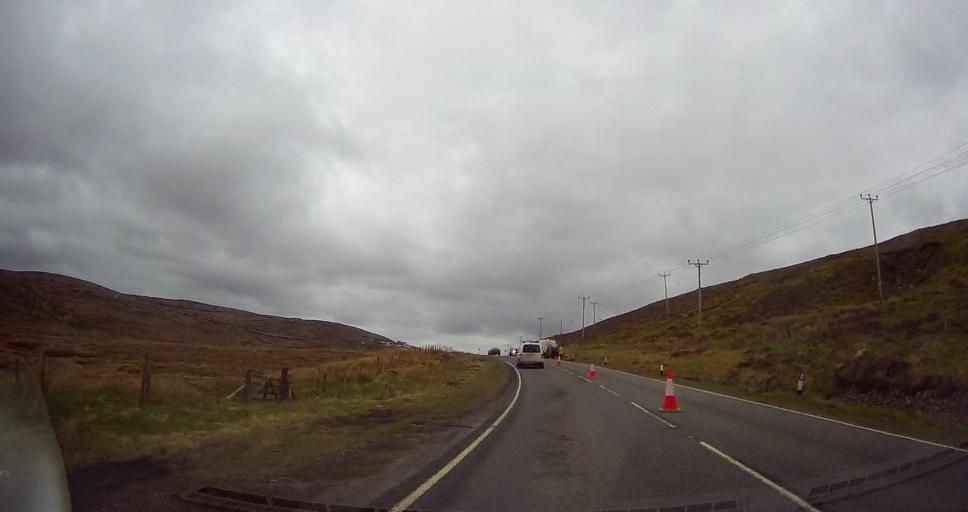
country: GB
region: Scotland
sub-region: Shetland Islands
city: Lerwick
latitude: 60.3346
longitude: -1.2537
